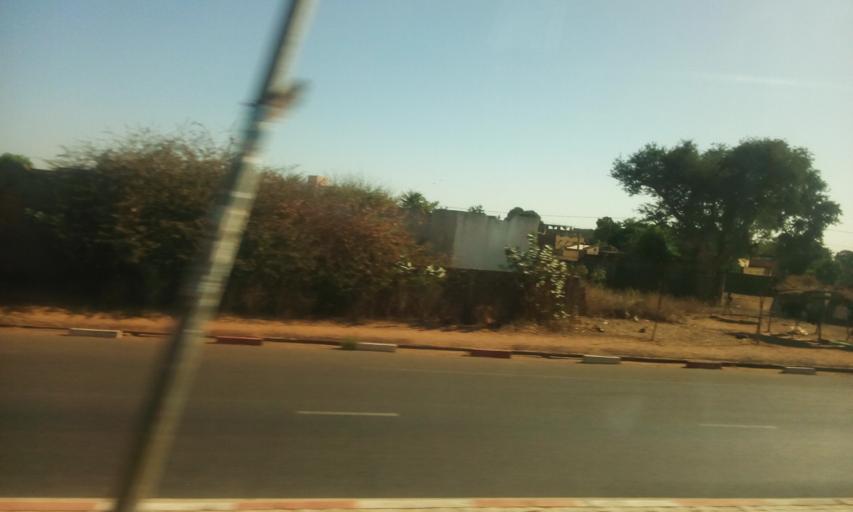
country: ML
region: Segou
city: Segou
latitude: 13.4157
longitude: -6.3149
